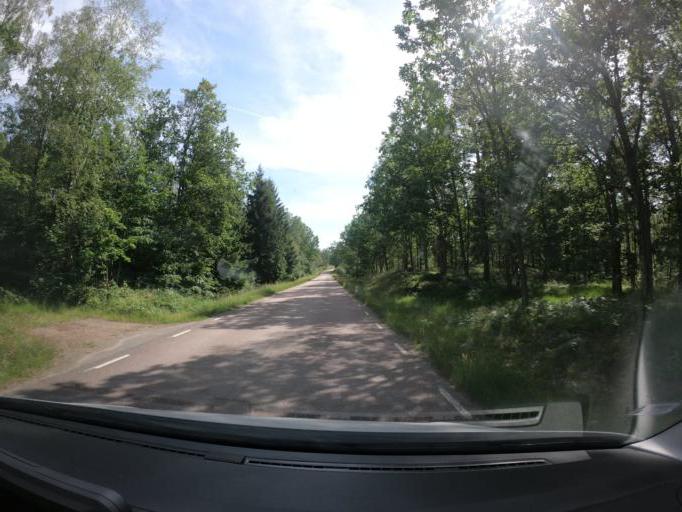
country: SE
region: Skane
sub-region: Orkelljunga Kommun
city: OErkelljunga
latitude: 56.3356
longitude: 13.3483
